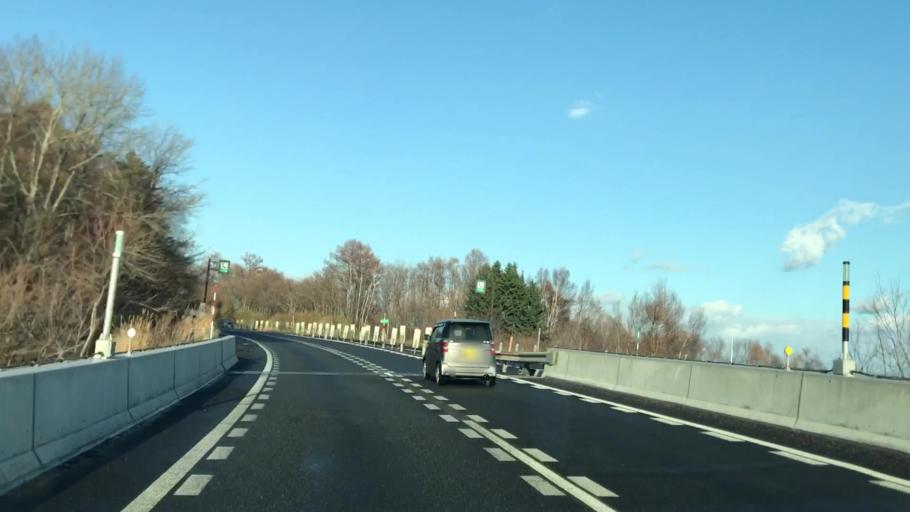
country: JP
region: Hokkaido
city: Otaru
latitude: 43.1511
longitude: 141.1273
